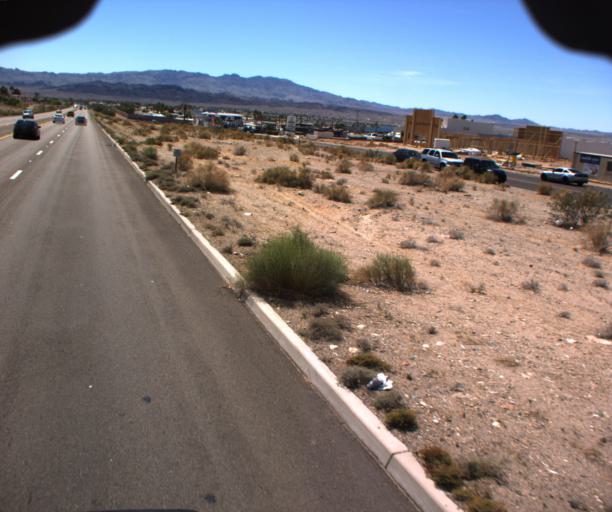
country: US
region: Arizona
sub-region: Mohave County
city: Lake Havasu City
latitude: 34.4919
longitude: -114.3494
